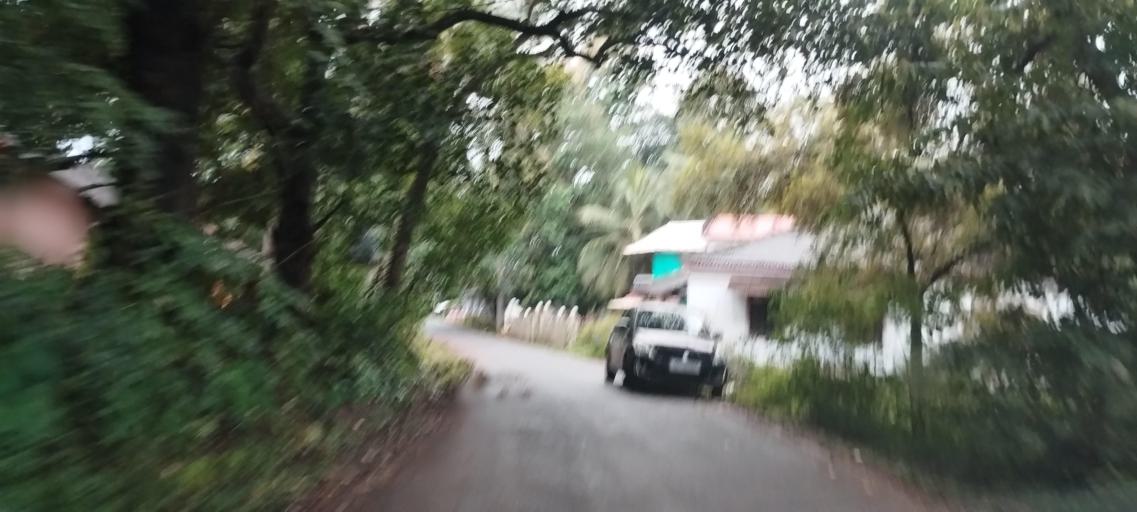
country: IN
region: Goa
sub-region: North Goa
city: Jua
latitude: 15.5244
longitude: 73.9023
